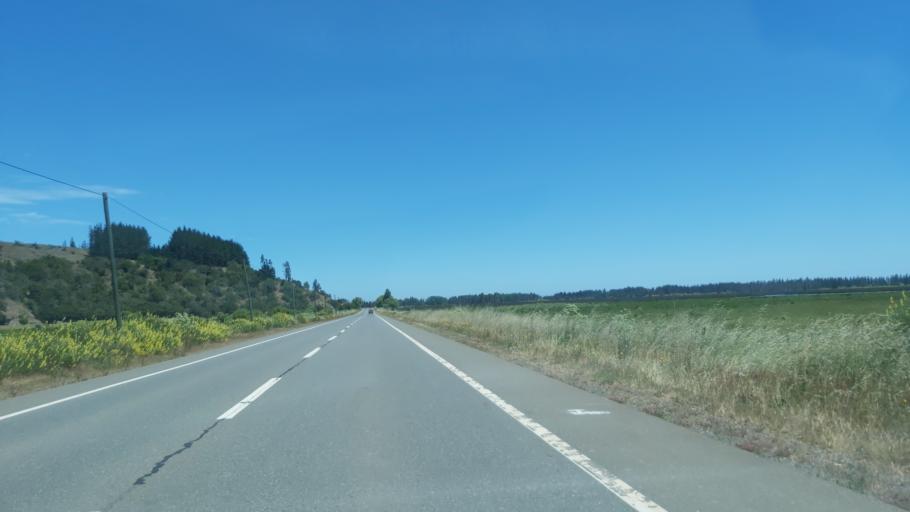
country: CL
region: Maule
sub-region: Provincia de Talca
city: Constitucion
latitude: -35.1546
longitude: -72.2341
